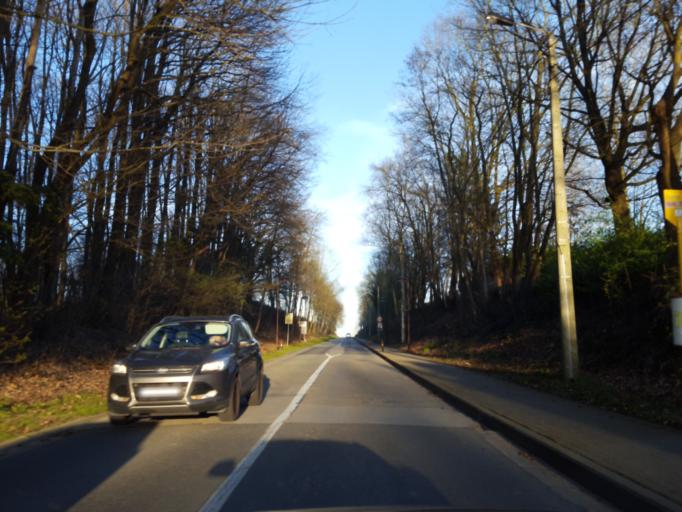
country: BE
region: Wallonia
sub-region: Province du Brabant Wallon
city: Mont-Saint-Guibert
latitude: 50.6416
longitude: 4.6292
